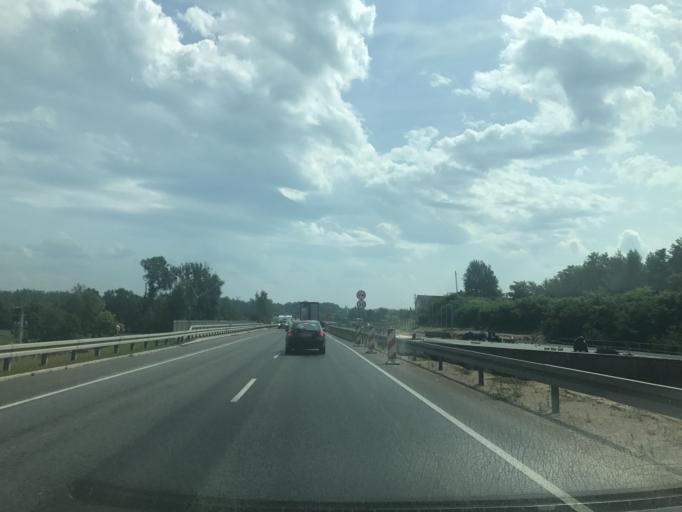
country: PL
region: Warmian-Masurian Voivodeship
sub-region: Powiat ostrodzki
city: Ostroda
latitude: 53.6987
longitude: 19.9817
